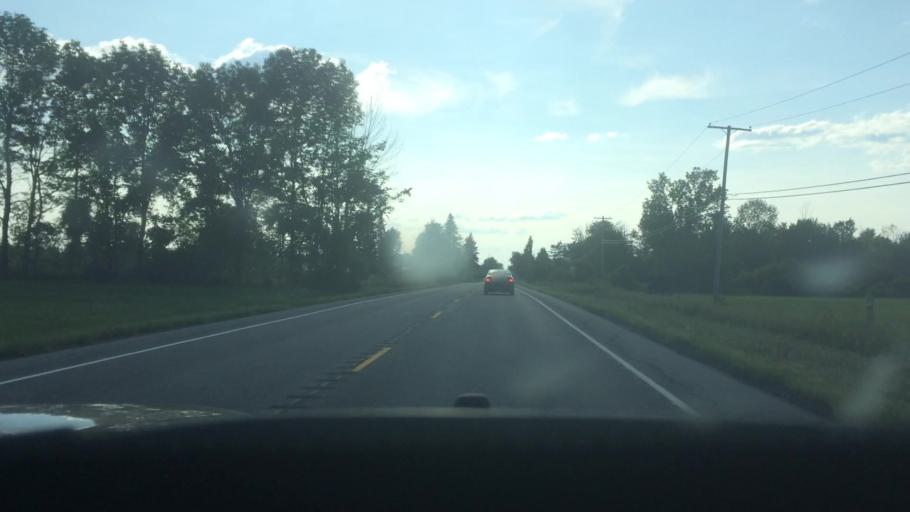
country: US
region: New York
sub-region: St. Lawrence County
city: Potsdam
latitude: 44.6877
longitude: -74.7708
